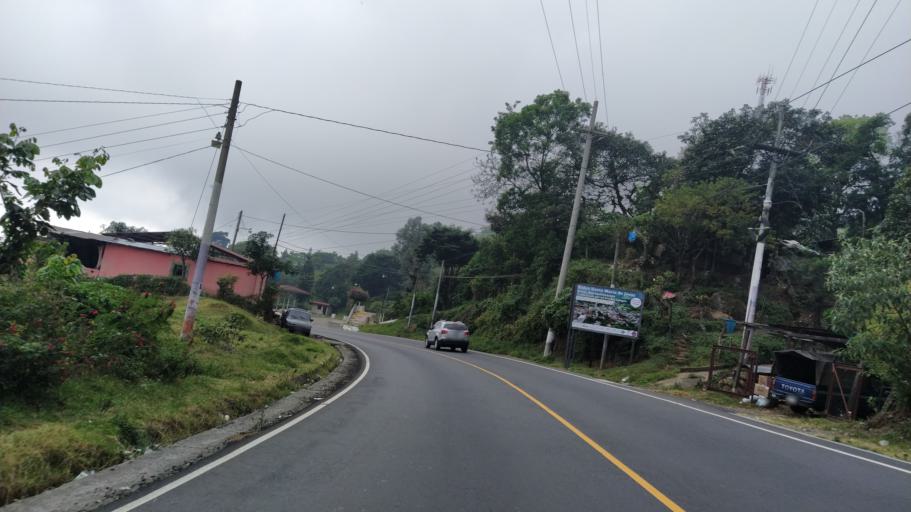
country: GT
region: Quetzaltenango
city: Zunil
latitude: 14.7258
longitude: -91.5272
